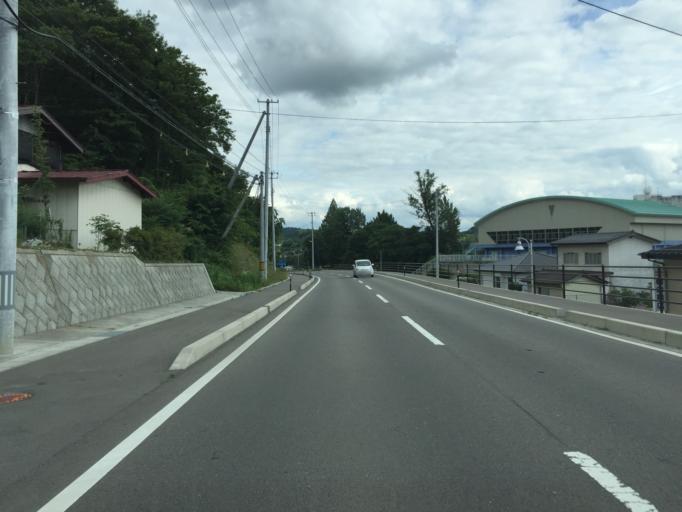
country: JP
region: Fukushima
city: Fukushima-shi
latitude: 37.6607
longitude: 140.5320
